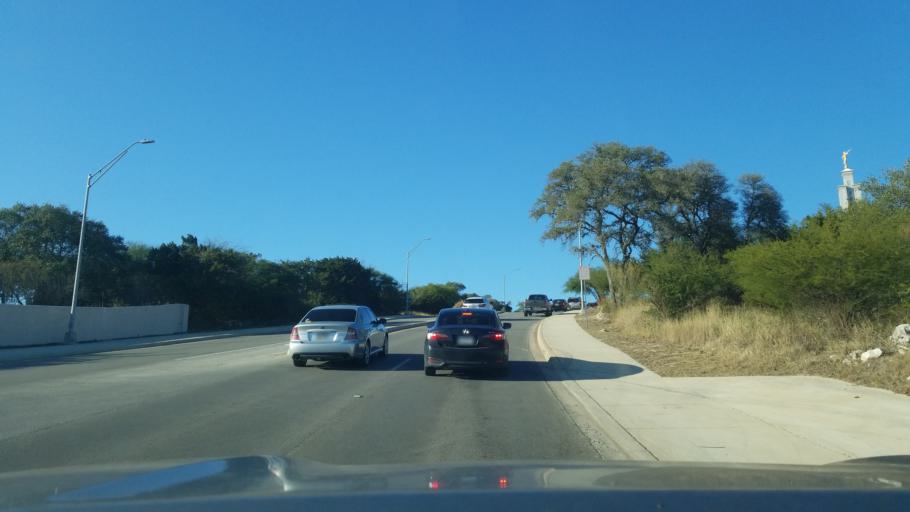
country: US
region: Texas
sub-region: Bexar County
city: Hollywood Park
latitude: 29.6399
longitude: -98.4887
